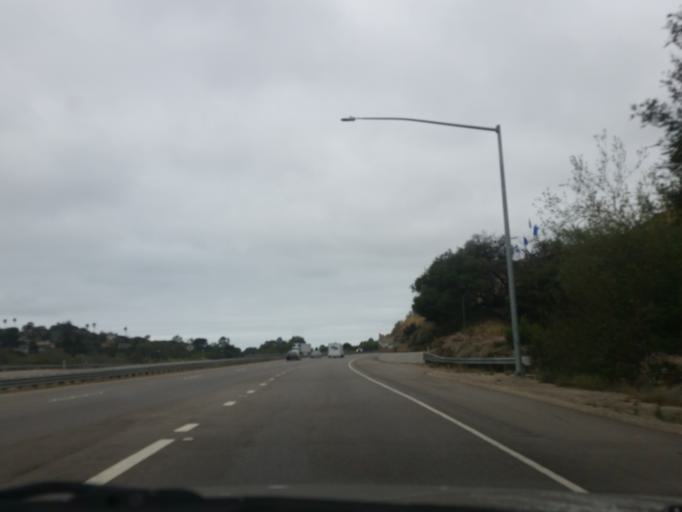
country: US
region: California
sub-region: San Luis Obispo County
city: Grover Beach
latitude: 35.1307
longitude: -120.6084
